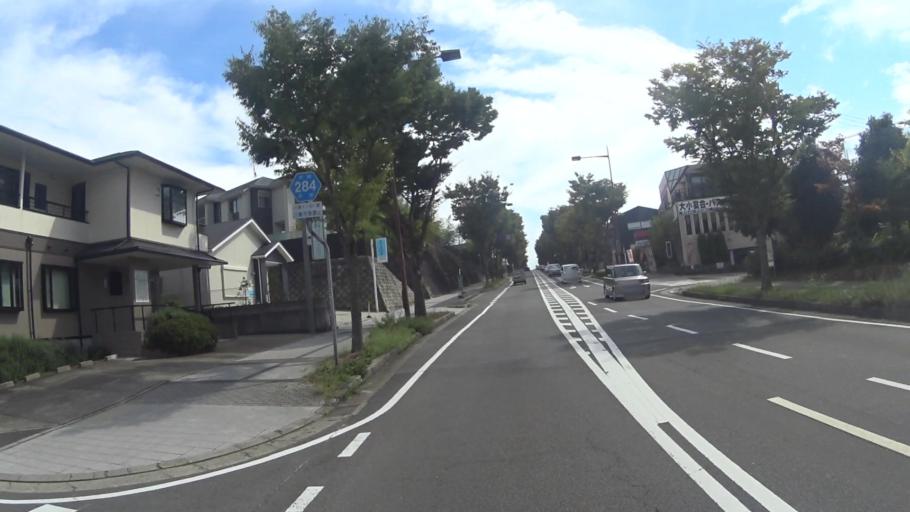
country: JP
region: Kyoto
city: Yawata
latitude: 34.8490
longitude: 135.7125
